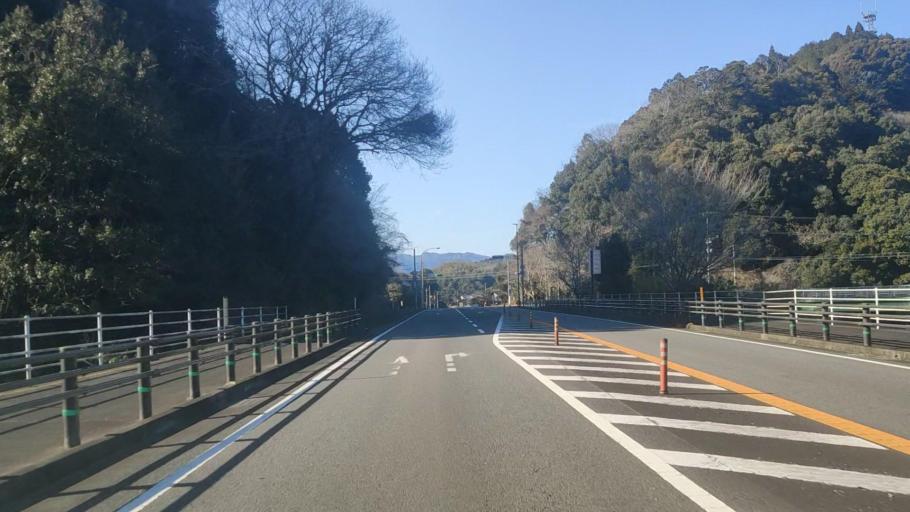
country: JP
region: Oita
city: Usuki
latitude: 33.0615
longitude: 131.6675
